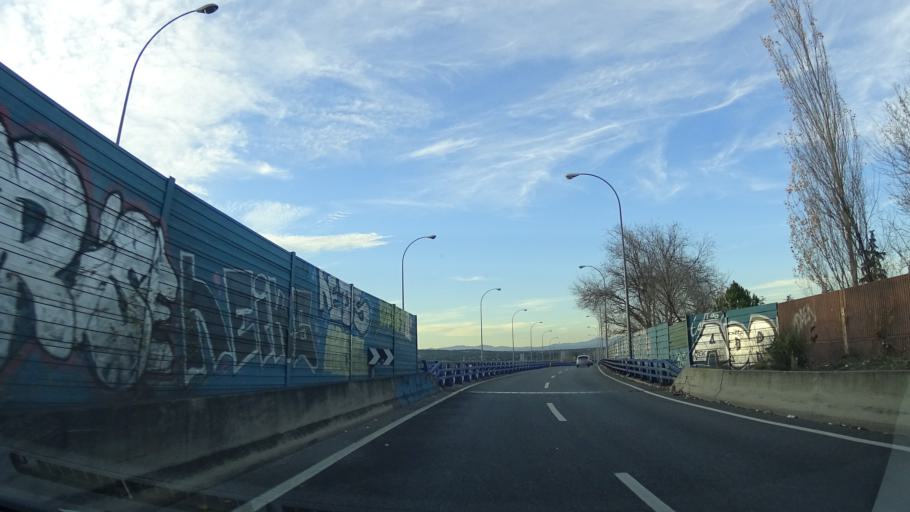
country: ES
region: Madrid
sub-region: Provincia de Madrid
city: Fuencarral-El Pardo
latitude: 40.4748
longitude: -3.7495
